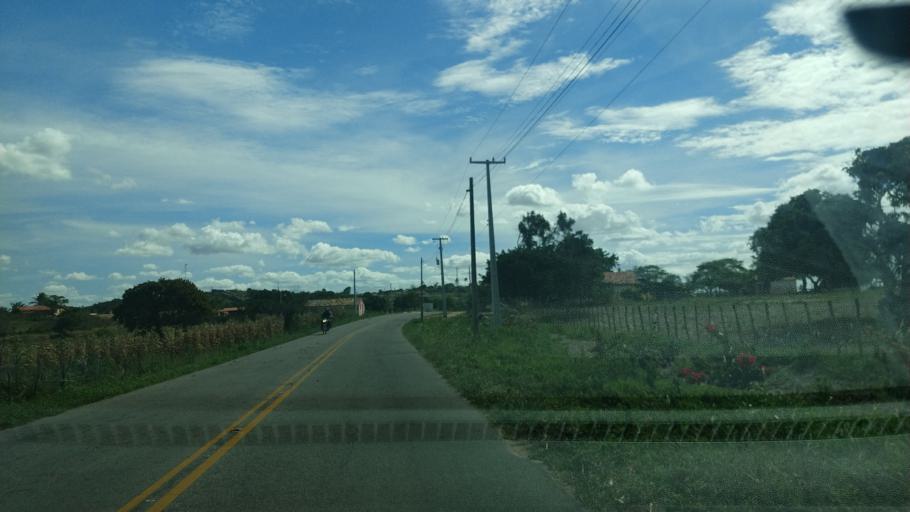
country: BR
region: Rio Grande do Norte
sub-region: Sao Jose Do Campestre
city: Sao Jose do Campestre
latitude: -6.4197
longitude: -35.7211
